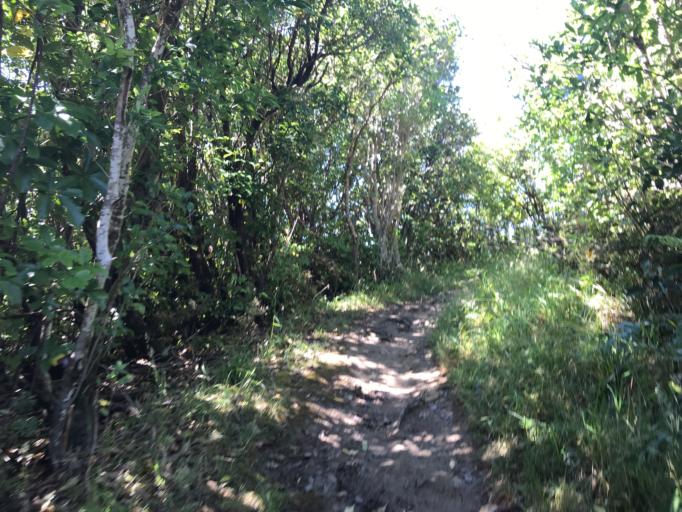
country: NZ
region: Marlborough
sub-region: Marlborough District
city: Picton
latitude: -41.2053
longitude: 174.0256
